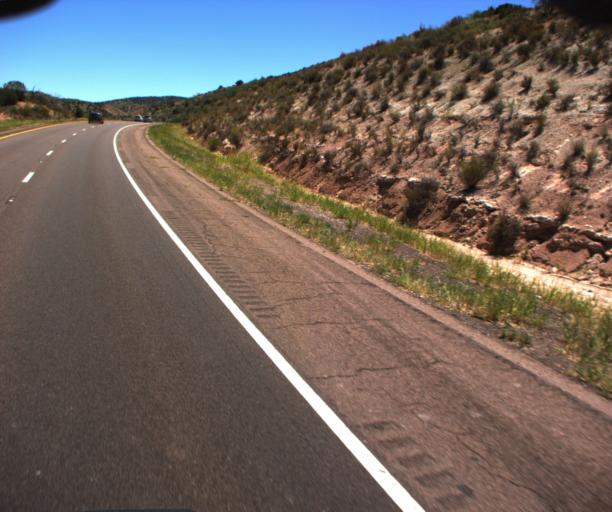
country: US
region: Arizona
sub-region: Gila County
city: Tonto Basin
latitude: 34.0226
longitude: -111.3613
